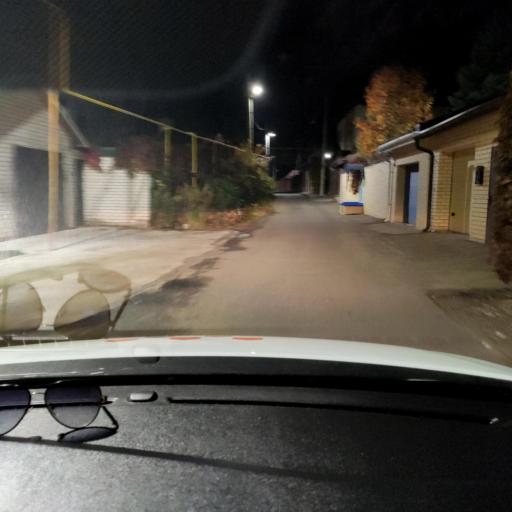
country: RU
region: Tatarstan
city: Verkhniy Uslon
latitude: 55.6222
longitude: 49.0176
